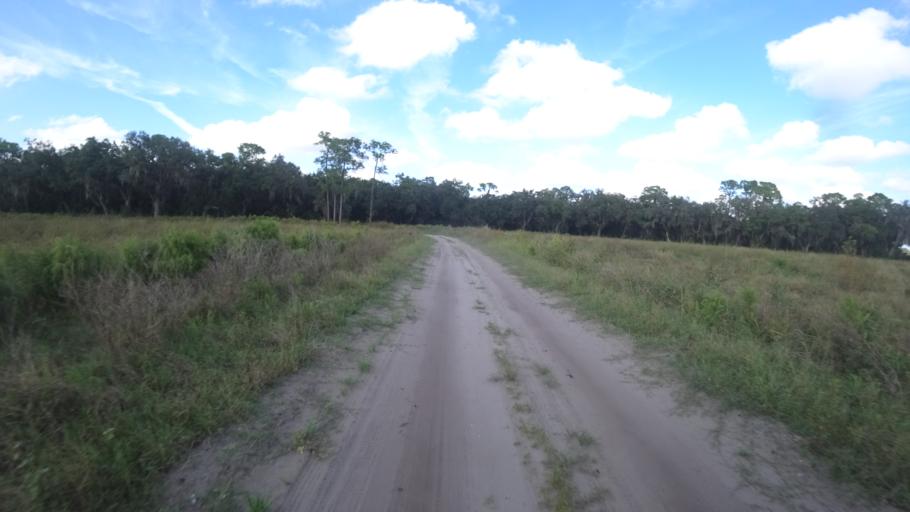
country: US
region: Florida
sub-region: DeSoto County
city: Arcadia
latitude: 27.3480
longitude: -82.1146
